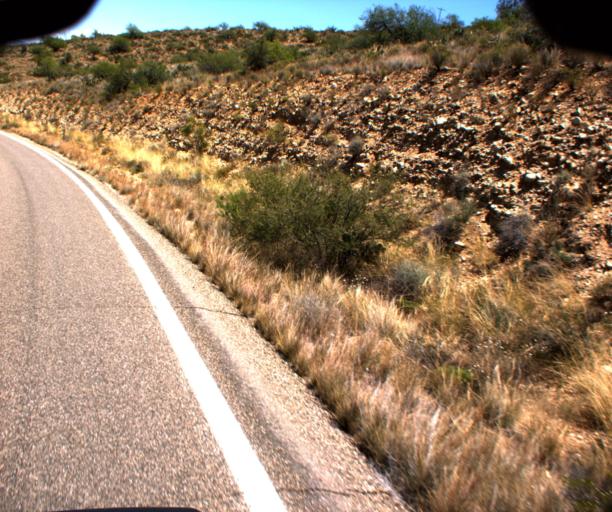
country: US
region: Arizona
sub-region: Yavapai County
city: Bagdad
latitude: 34.5204
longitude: -113.1013
